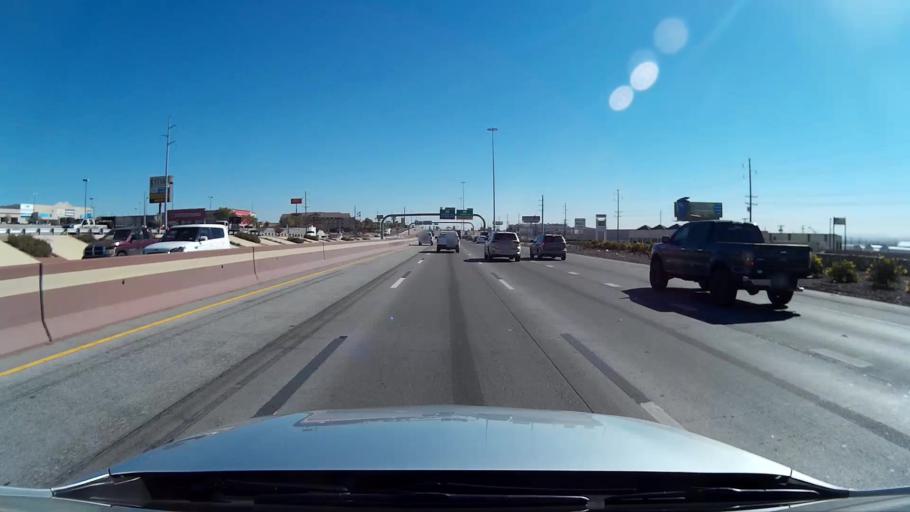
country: US
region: Texas
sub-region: El Paso County
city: Socorro
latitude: 31.7298
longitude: -106.3145
